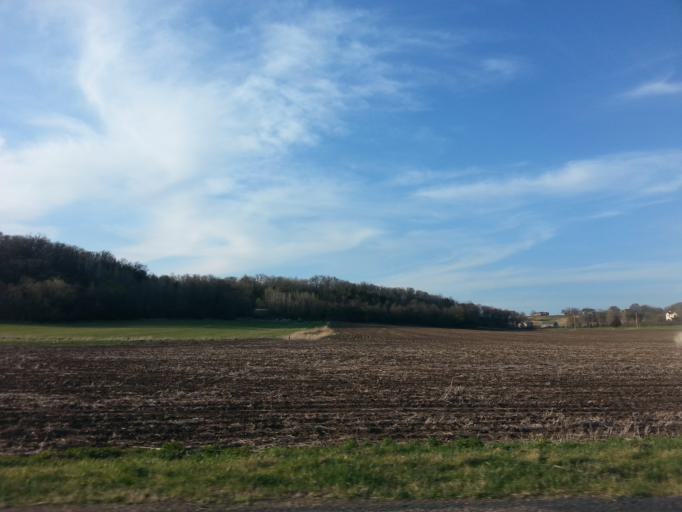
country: US
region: Wisconsin
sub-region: Pierce County
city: River Falls
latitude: 44.8870
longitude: -92.6715
